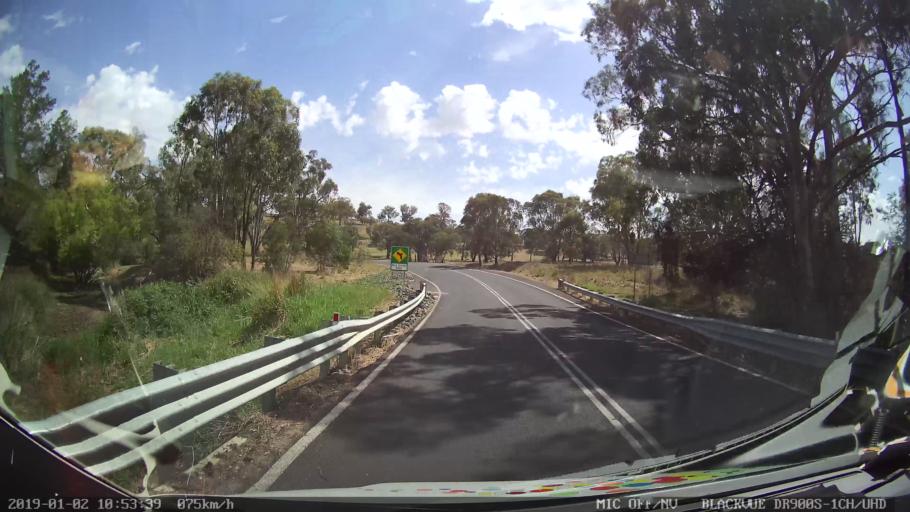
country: AU
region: New South Wales
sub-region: Cootamundra
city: Cootamundra
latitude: -34.6763
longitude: 148.2776
